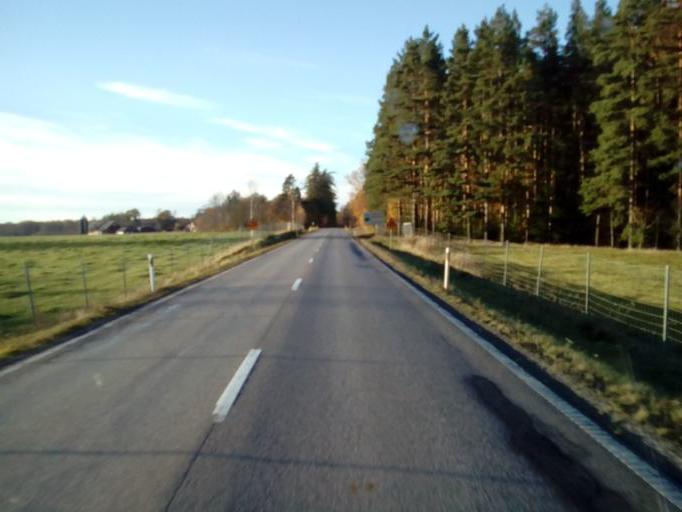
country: SE
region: OErebro
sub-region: Hallsbergs Kommun
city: Palsboda
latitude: 59.0105
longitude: 15.3967
